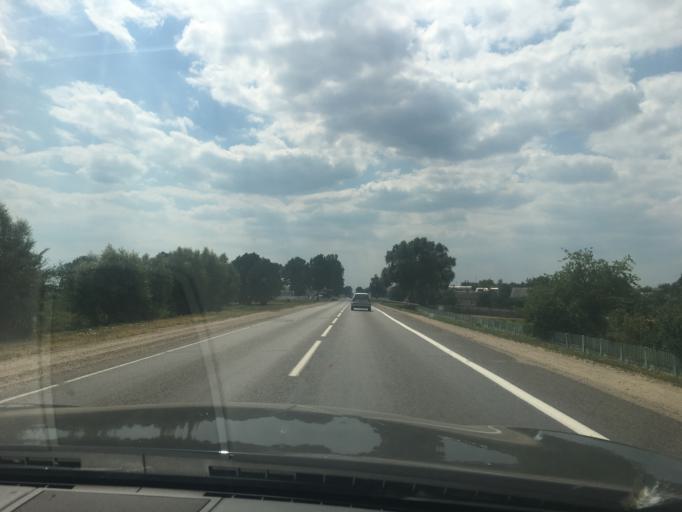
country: BY
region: Brest
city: Pruzhany
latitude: 52.5494
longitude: 24.4661
